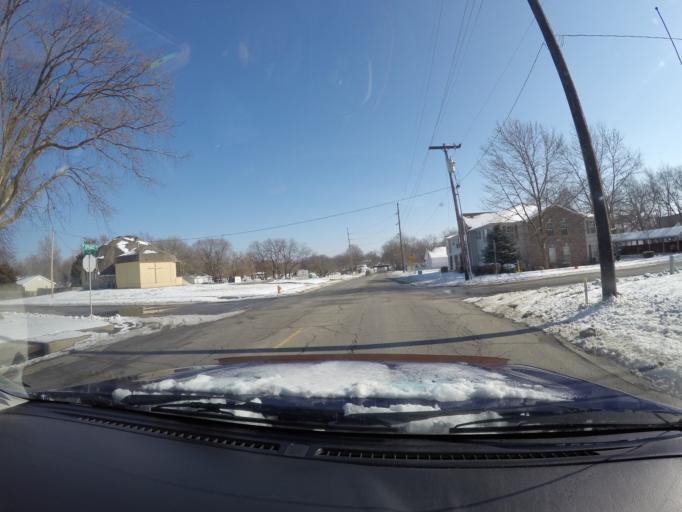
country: US
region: Kansas
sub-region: Johnson County
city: Olathe
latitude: 38.8865
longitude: -94.8244
